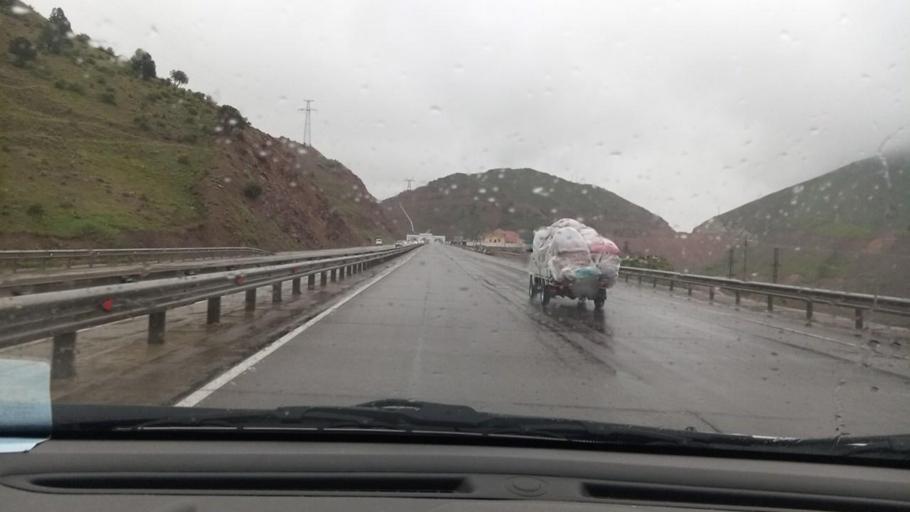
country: UZ
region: Toshkent
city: Angren
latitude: 41.0847
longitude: 70.5395
